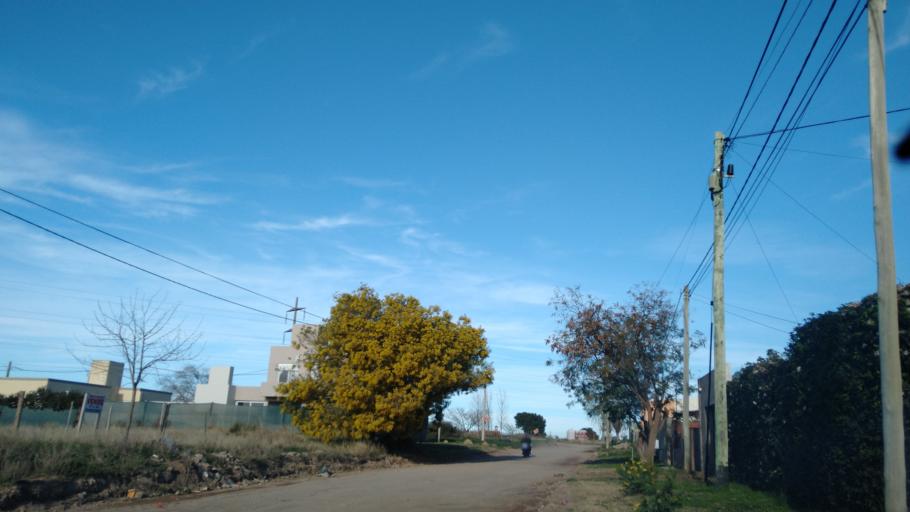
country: AR
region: Buenos Aires
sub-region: Partido de Bahia Blanca
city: Bahia Blanca
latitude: -38.7040
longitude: -62.2069
